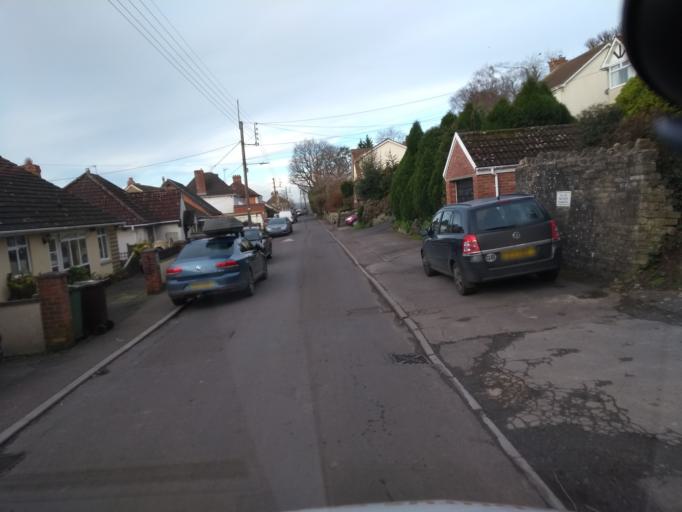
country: GB
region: England
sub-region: Somerset
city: Glastonbury
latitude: 51.1390
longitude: -2.7294
